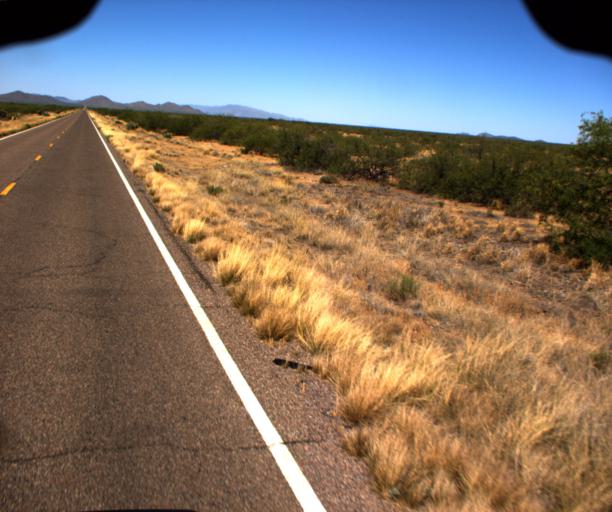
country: US
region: Arizona
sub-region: Yavapai County
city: Congress
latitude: 34.1515
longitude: -112.8799
